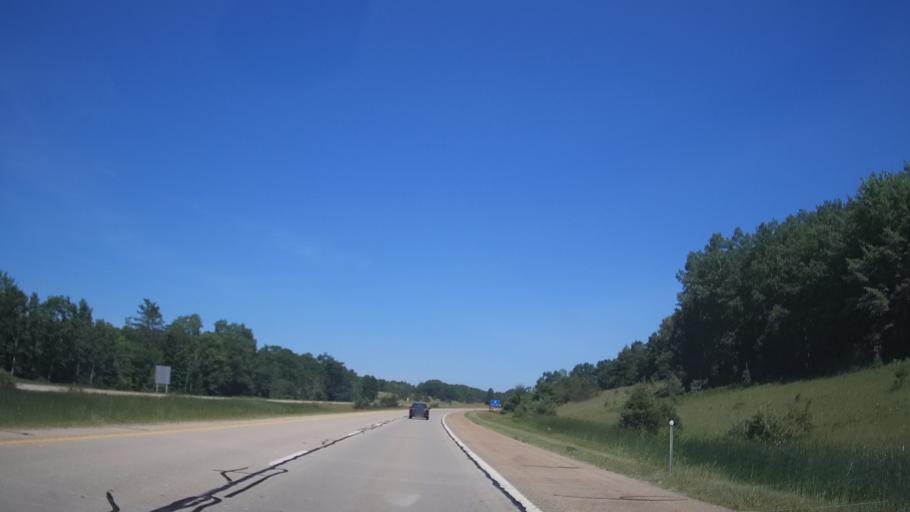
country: US
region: Michigan
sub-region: Clare County
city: Clare
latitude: 43.8704
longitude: -84.8857
